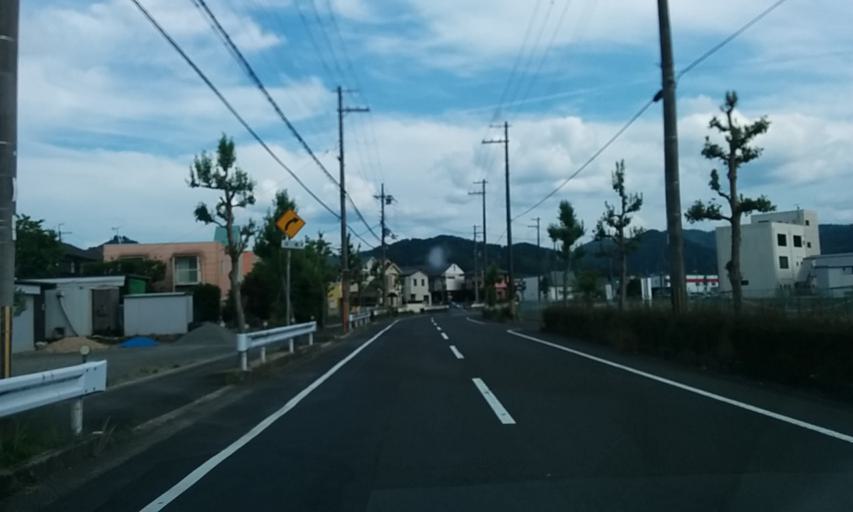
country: JP
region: Kyoto
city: Ayabe
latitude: 35.3070
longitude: 135.2616
